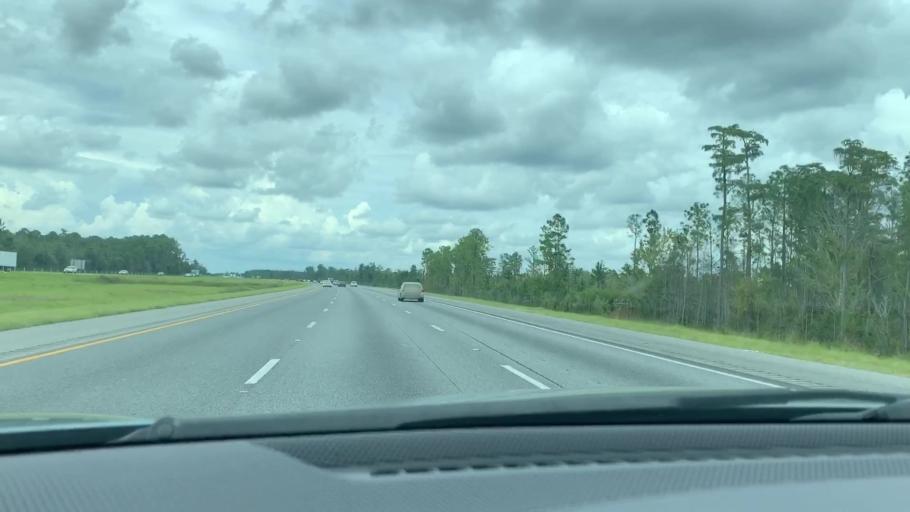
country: US
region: Georgia
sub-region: McIntosh County
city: Darien
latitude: 31.4152
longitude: -81.4434
